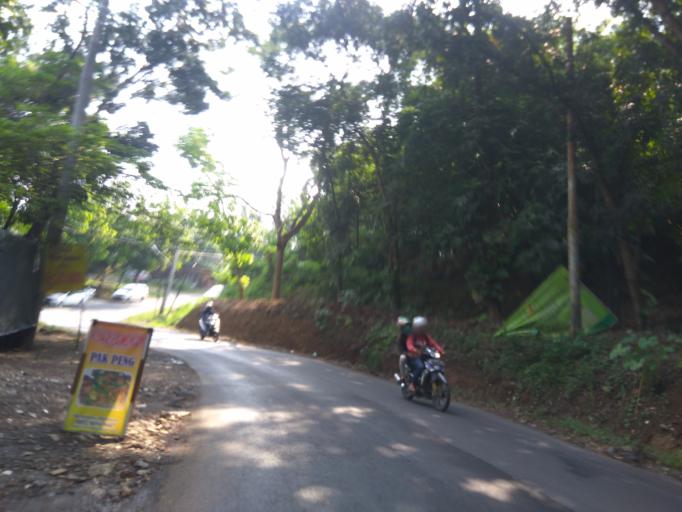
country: ID
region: Central Java
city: Semarang
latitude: -7.0227
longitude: 110.4002
